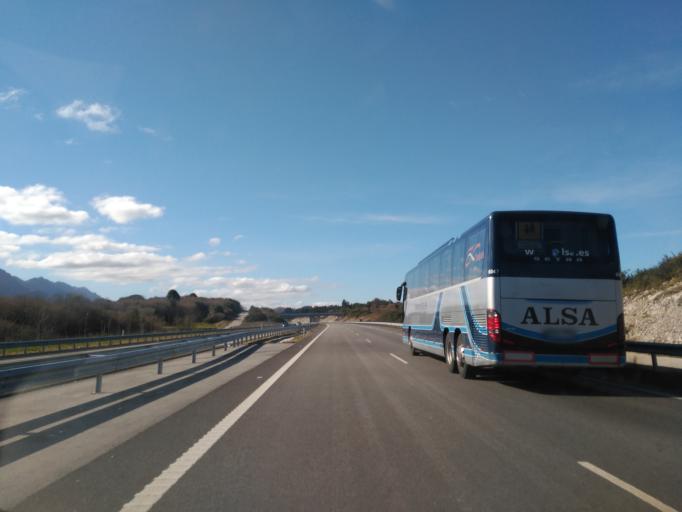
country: ES
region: Asturias
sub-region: Province of Asturias
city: Llanes
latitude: 43.4021
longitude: -4.6779
